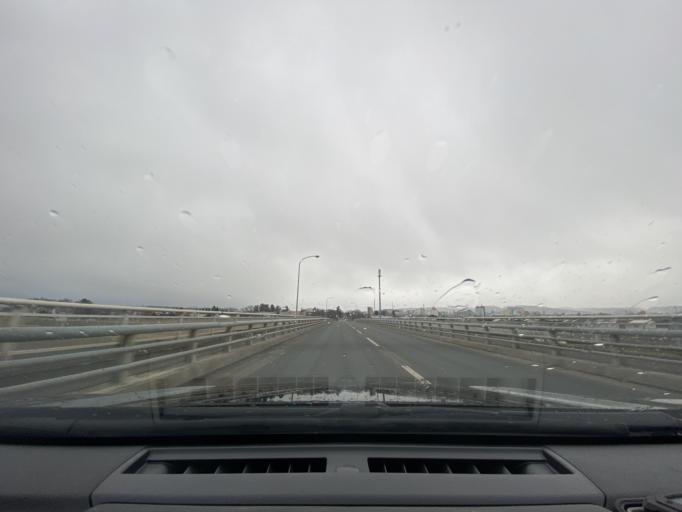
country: JP
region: Hokkaido
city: Kitami
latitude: 43.7991
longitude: 143.9102
